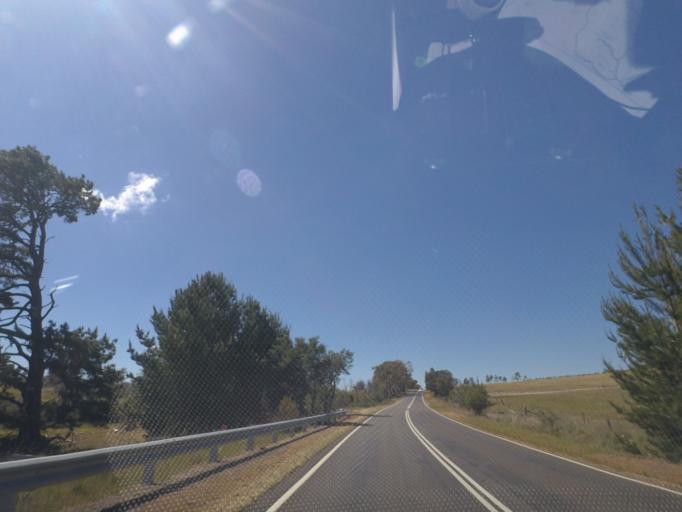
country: AU
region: Victoria
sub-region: Hume
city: Sunbury
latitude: -37.0850
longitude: 144.7596
